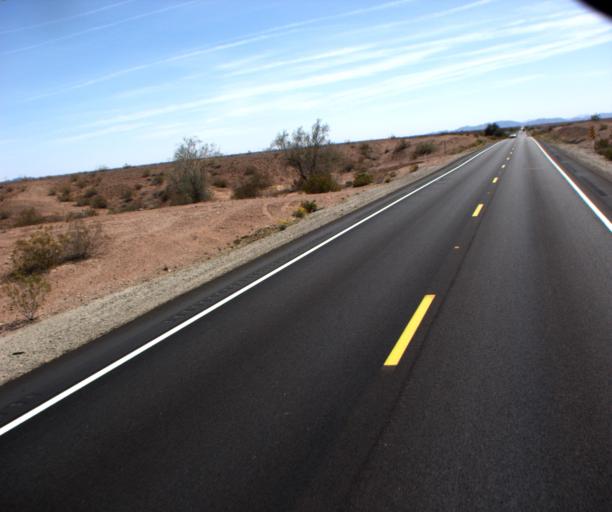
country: US
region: Arizona
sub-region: Yuma County
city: Wellton
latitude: 33.0544
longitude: -114.2918
